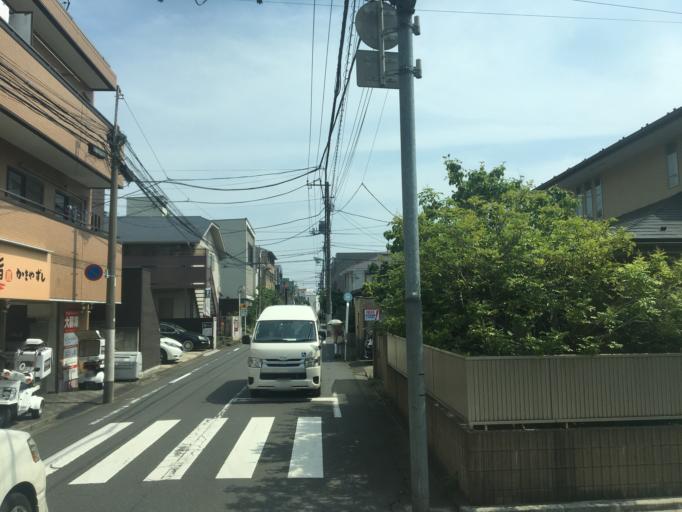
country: JP
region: Tokyo
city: Tokyo
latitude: 35.7384
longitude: 139.6938
